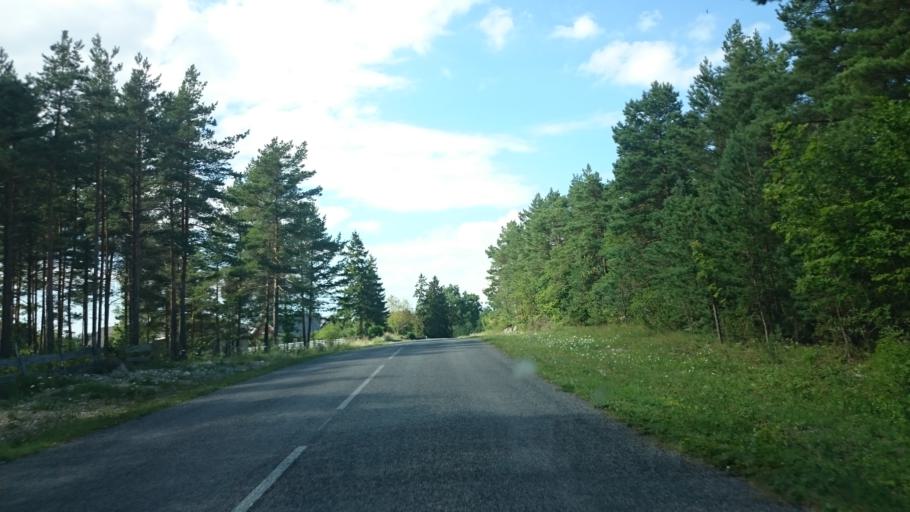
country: EE
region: Saare
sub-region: Orissaare vald
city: Orissaare
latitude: 58.5999
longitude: 22.9787
